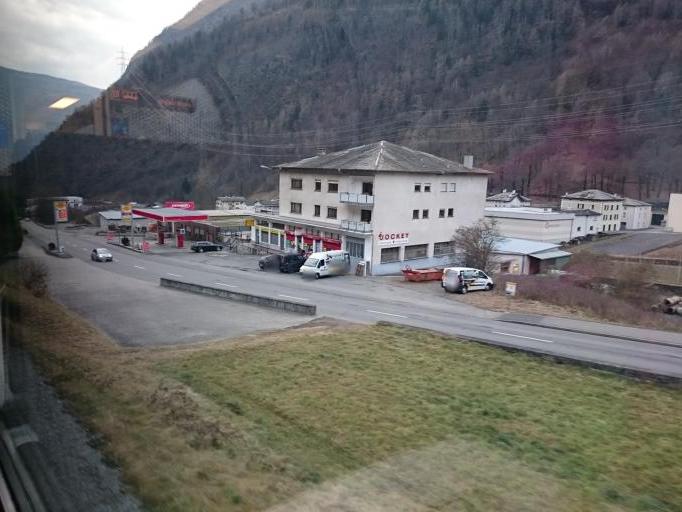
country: CH
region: Grisons
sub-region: Bernina District
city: Brusio
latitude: 46.2423
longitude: 10.1331
